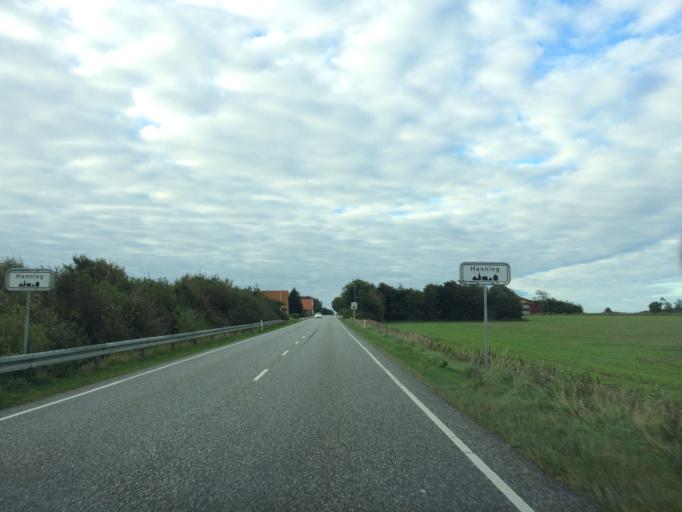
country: DK
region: Central Jutland
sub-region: Ringkobing-Skjern Kommune
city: Skjern
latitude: 56.0204
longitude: 8.5027
